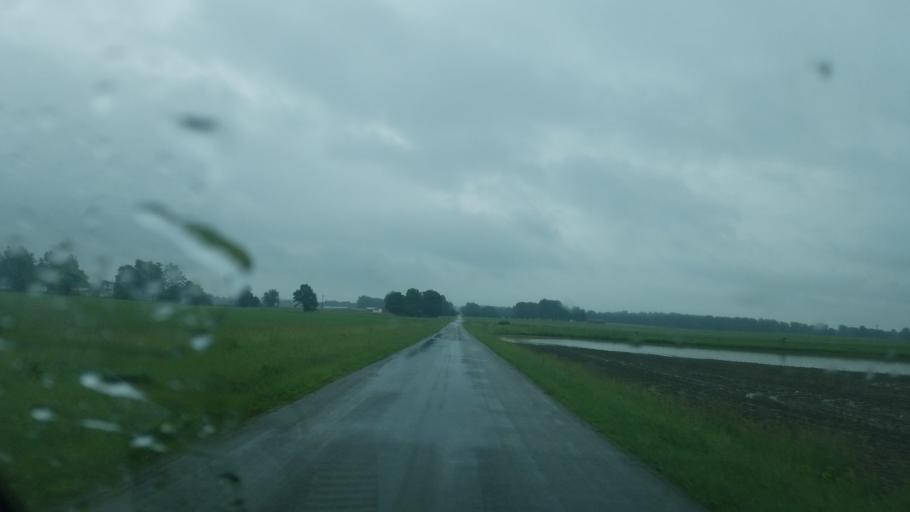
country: US
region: Ohio
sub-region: Huron County
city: Plymouth
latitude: 40.9453
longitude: -82.7488
